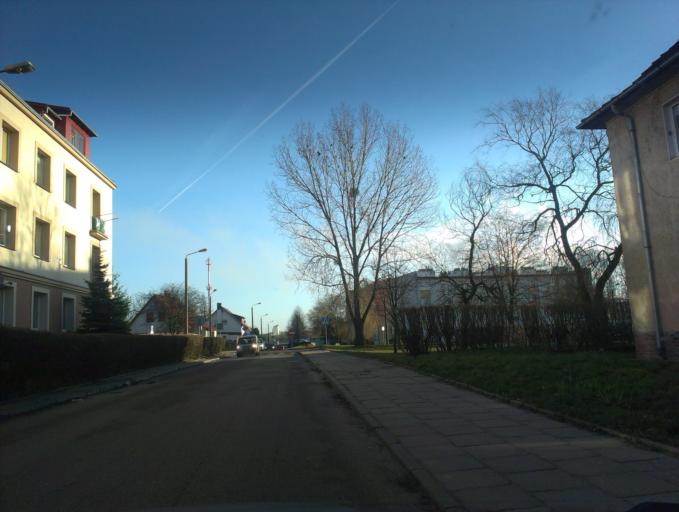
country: PL
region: West Pomeranian Voivodeship
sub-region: Powiat szczecinecki
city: Szczecinek
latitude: 53.6999
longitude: 16.7033
